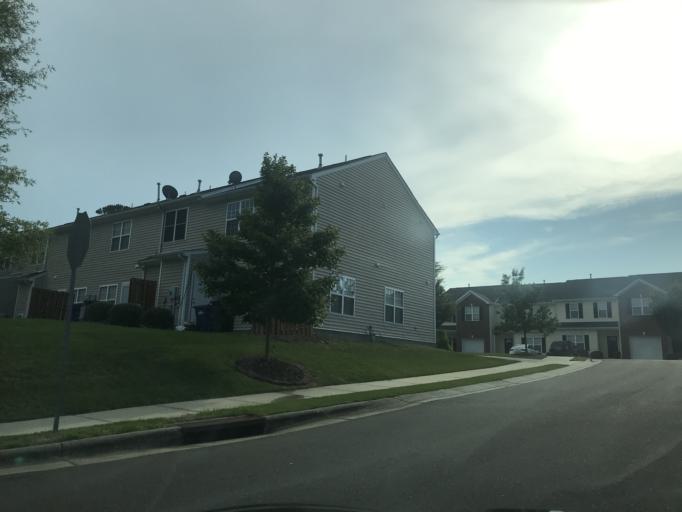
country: US
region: North Carolina
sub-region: Wake County
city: Raleigh
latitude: 35.8276
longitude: -78.5881
